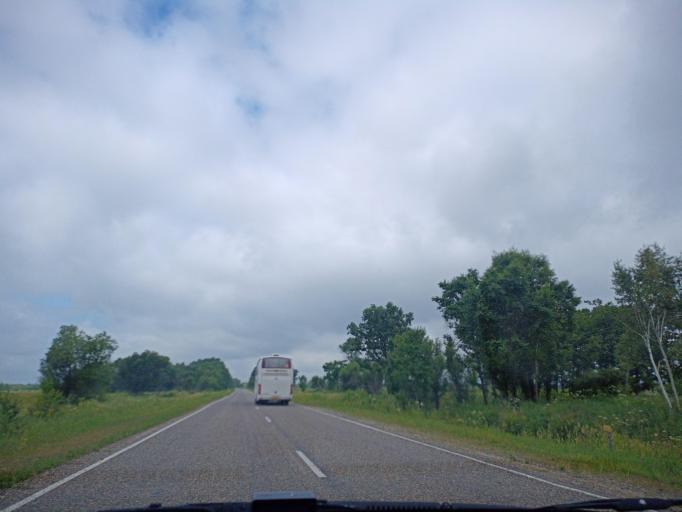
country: RU
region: Primorskiy
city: Novopokrovka
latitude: 45.9745
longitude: 134.2096
